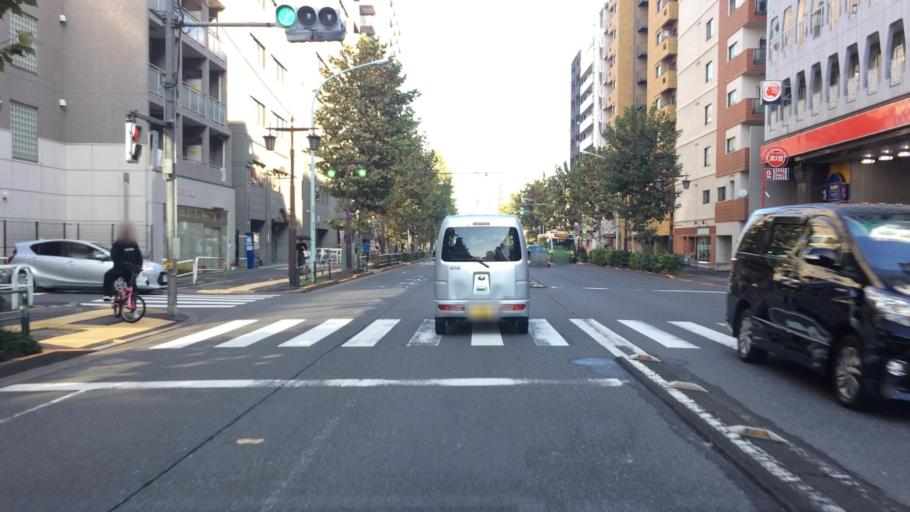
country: JP
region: Tokyo
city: Tokyo
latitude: 35.7033
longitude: 139.7084
